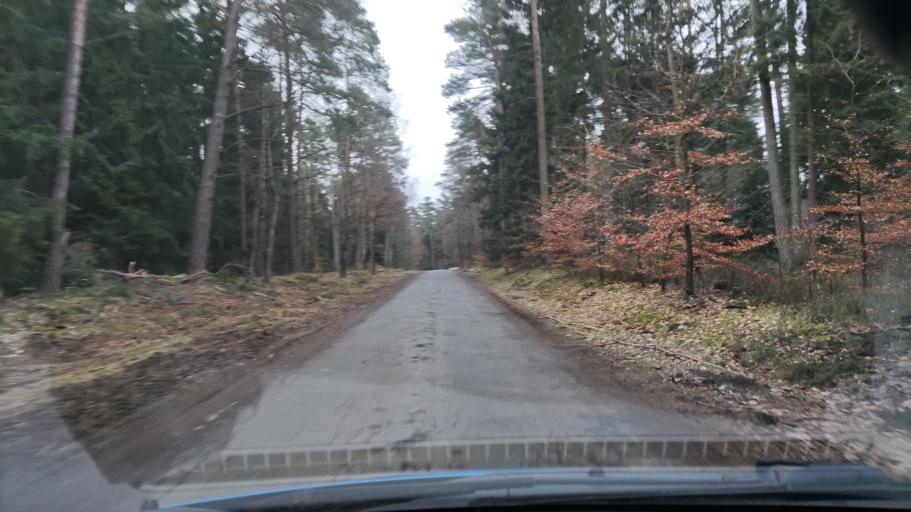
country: DE
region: Lower Saxony
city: Rehlingen
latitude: 53.0569
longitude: 10.2155
